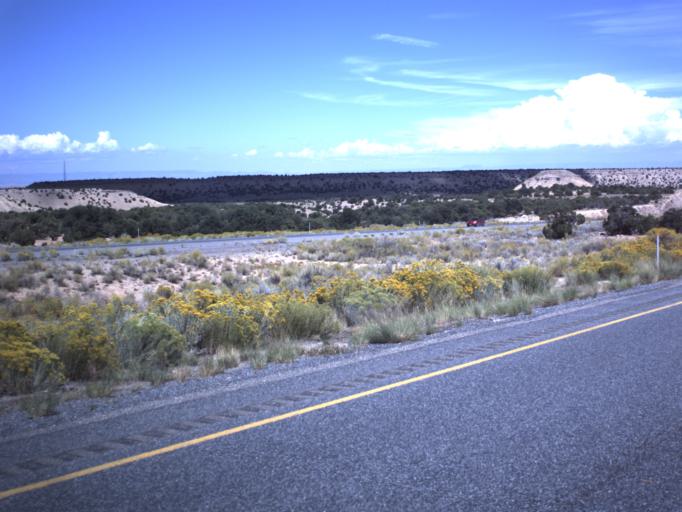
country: US
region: Utah
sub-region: Emery County
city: Castle Dale
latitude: 38.8977
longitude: -110.5785
